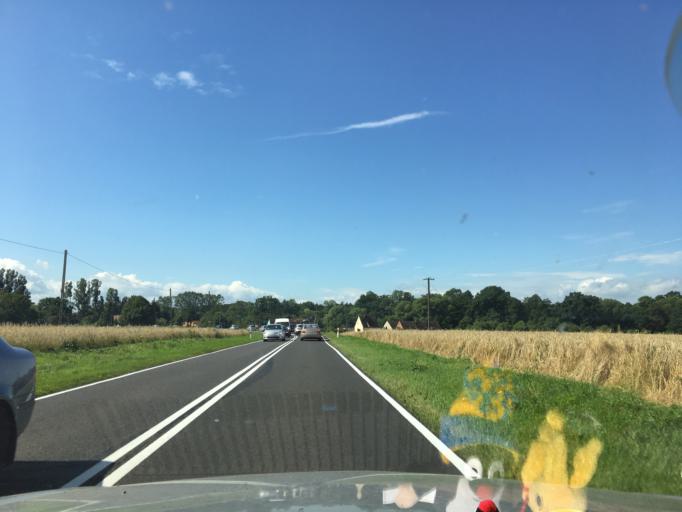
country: PL
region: West Pomeranian Voivodeship
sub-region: Powiat kamienski
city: Kamien Pomorski
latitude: 53.8623
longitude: 14.7616
